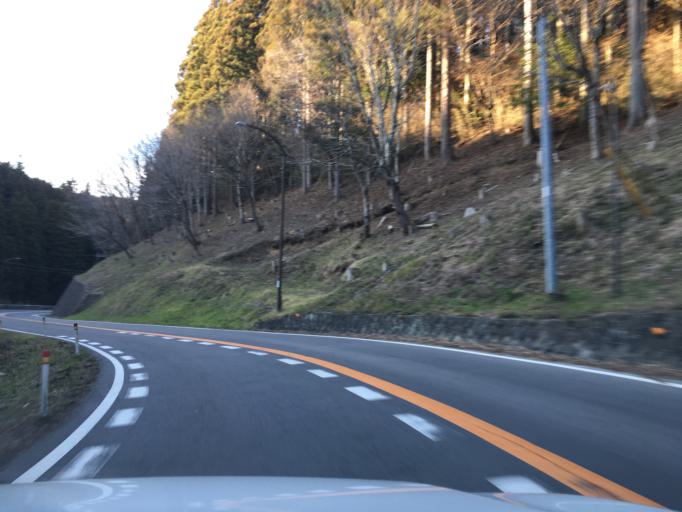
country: JP
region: Tochigi
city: Otawara
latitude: 36.8467
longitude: 140.1747
